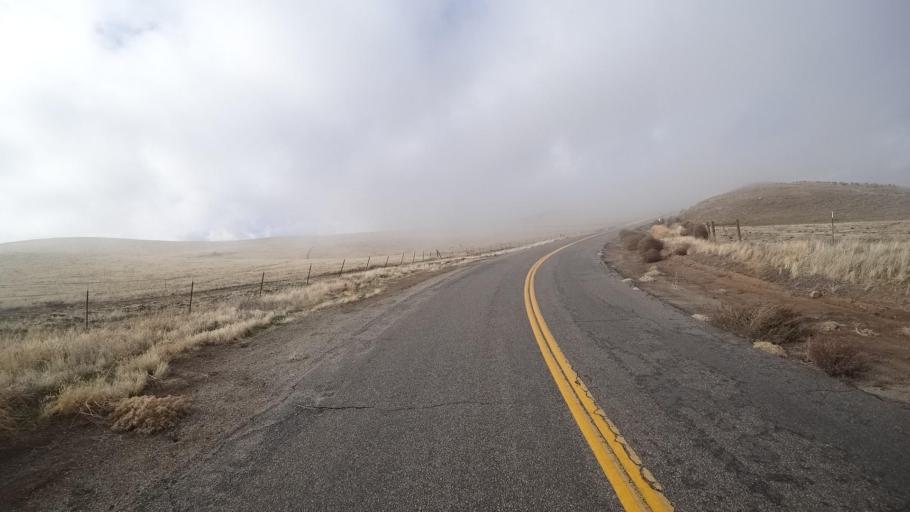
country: US
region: California
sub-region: Kern County
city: Maricopa
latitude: 34.9275
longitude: -119.4072
